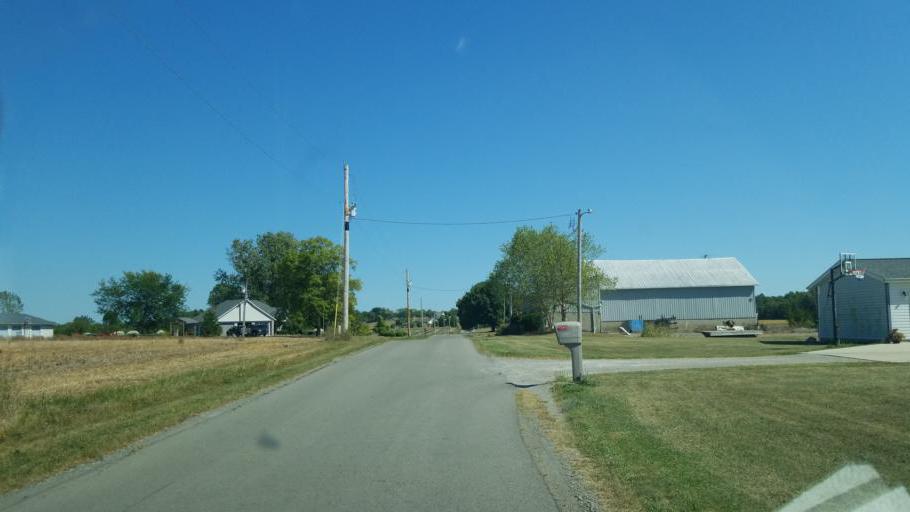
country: US
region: Ohio
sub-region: Logan County
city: Bellefontaine
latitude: 40.4244
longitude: -83.7953
